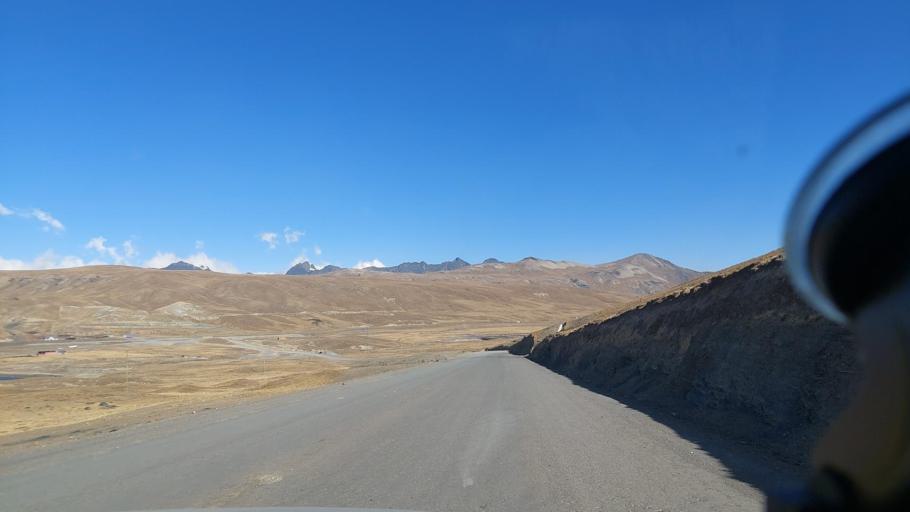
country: BO
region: La Paz
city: La Paz
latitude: -16.3415
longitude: -68.0476
